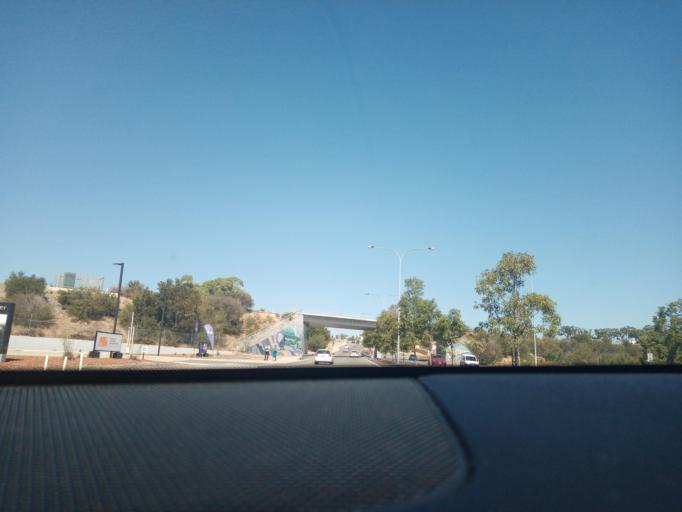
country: AU
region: Western Australia
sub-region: City of Cockburn
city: Beeliar
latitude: -32.1277
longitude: 115.7987
